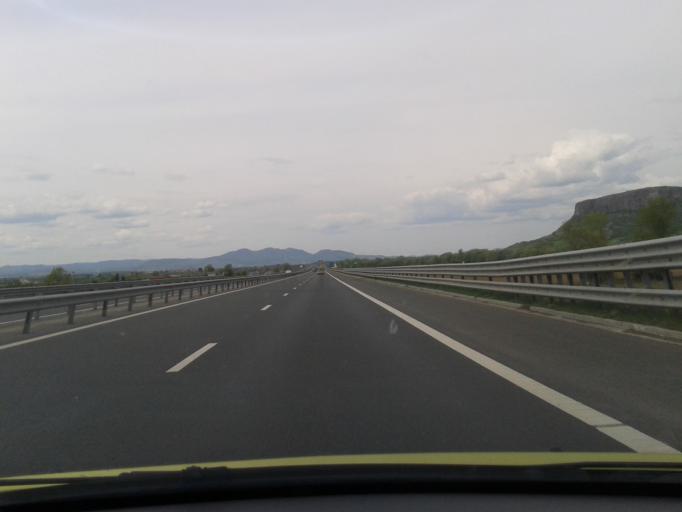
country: RO
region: Hunedoara
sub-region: Comuna Rapoltu Mare
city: Rapoltu Mare
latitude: 45.8446
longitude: 23.0695
